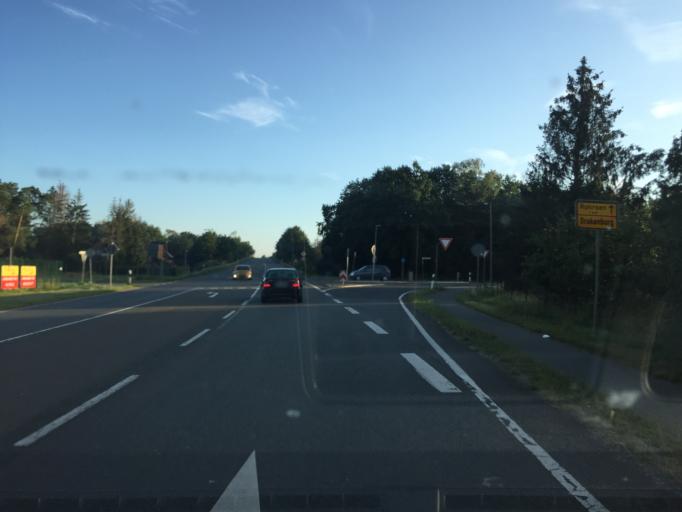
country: DE
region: Lower Saxony
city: Rohrsen
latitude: 52.6990
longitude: 9.2373
